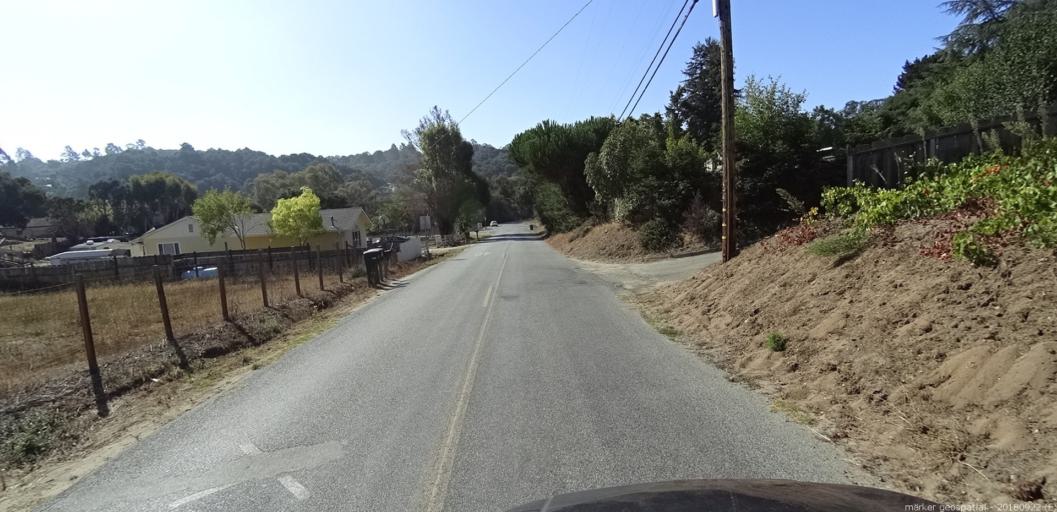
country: US
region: California
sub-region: Monterey County
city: Prunedale
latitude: 36.8092
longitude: -121.6496
